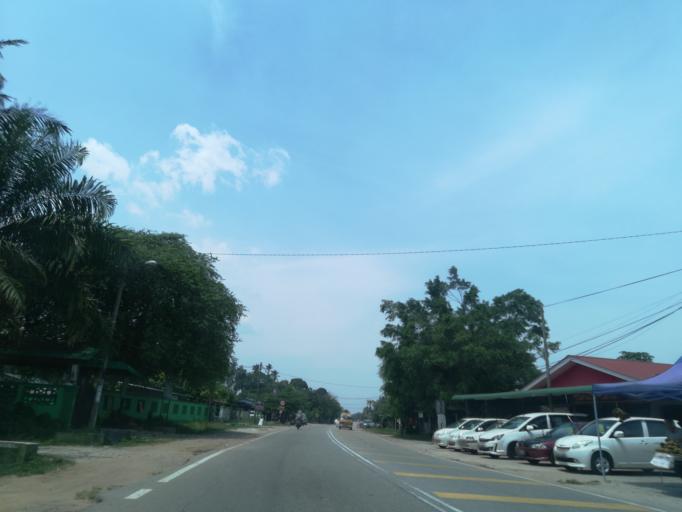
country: MY
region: Penang
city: Tasek Glugor
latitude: 5.4456
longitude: 100.5527
